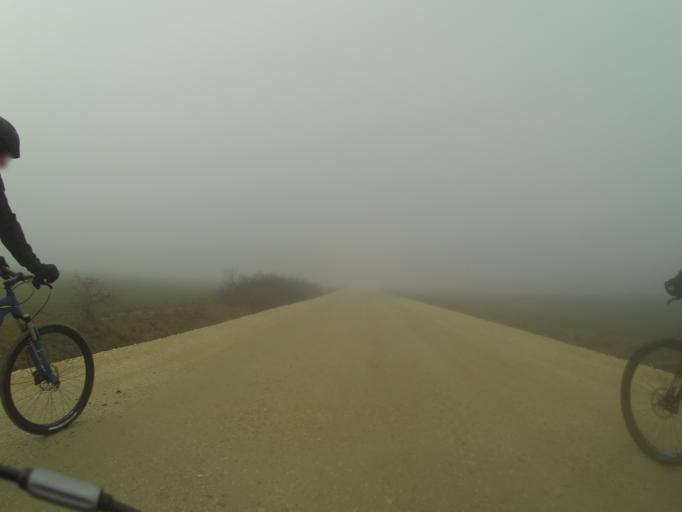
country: RO
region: Mehedinti
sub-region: Comuna Baclesu
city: Baclesu
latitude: 44.4409
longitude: 23.1334
